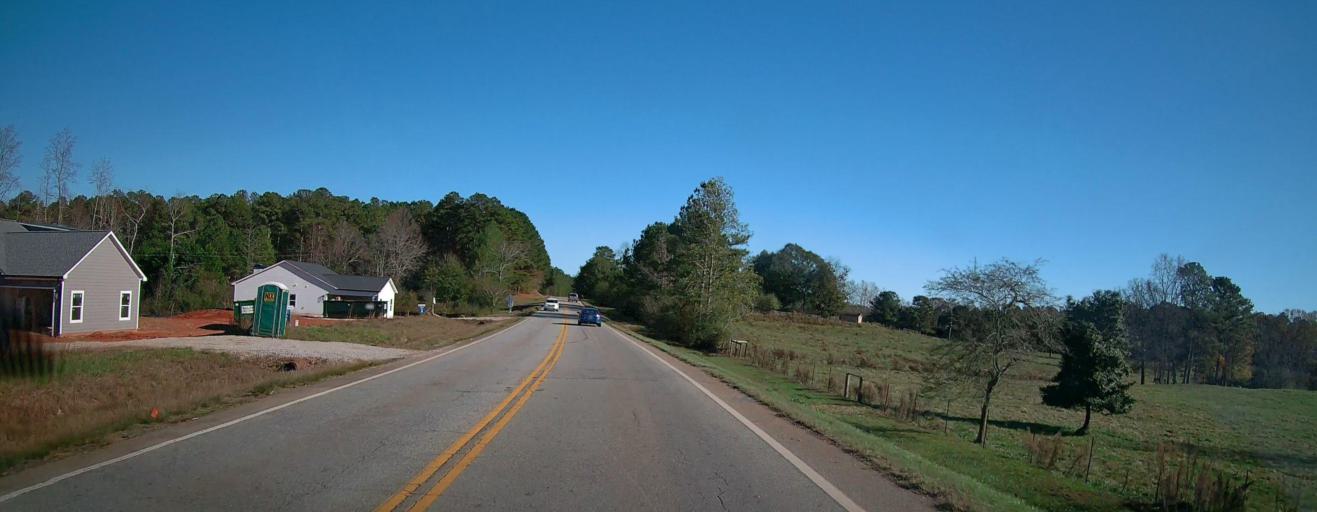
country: US
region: Georgia
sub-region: Hall County
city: Lula
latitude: 34.4437
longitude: -83.7263
